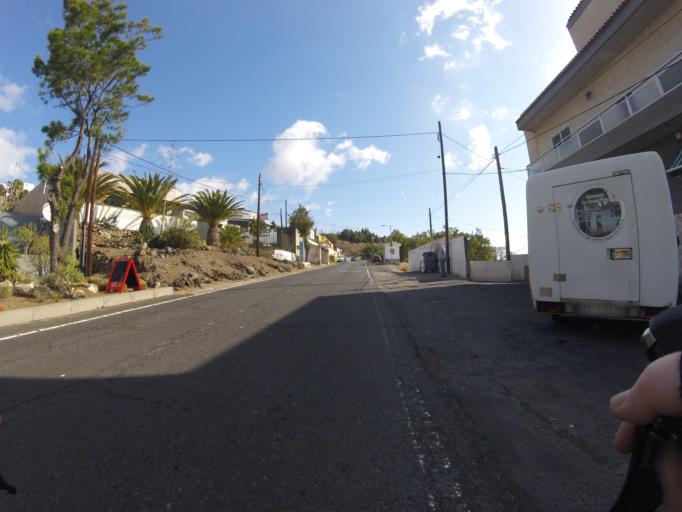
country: ES
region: Canary Islands
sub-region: Provincia de Santa Cruz de Tenerife
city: La Laguna
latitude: 28.4147
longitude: -16.3228
